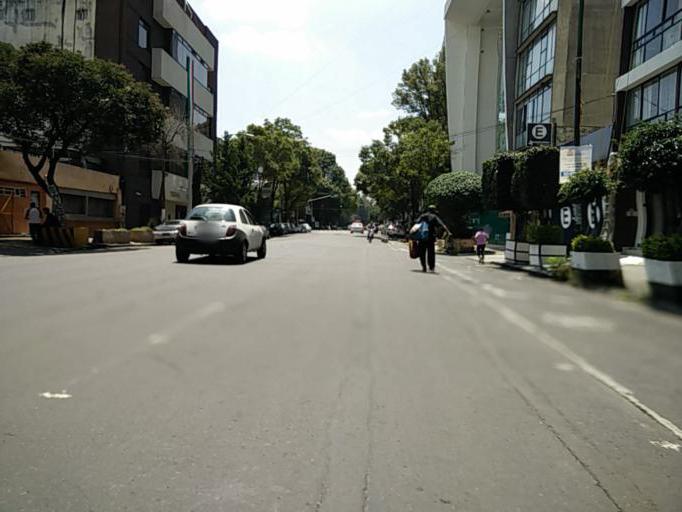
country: MX
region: Mexico City
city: Benito Juarez
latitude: 19.4238
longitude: -99.1611
